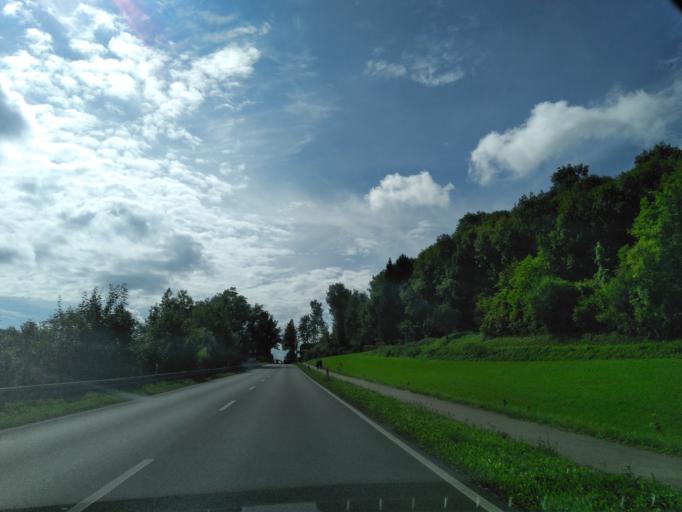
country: DE
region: Baden-Wuerttemberg
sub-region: Regierungsbezirk Stuttgart
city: Besigheim
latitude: 48.9756
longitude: 9.1439
